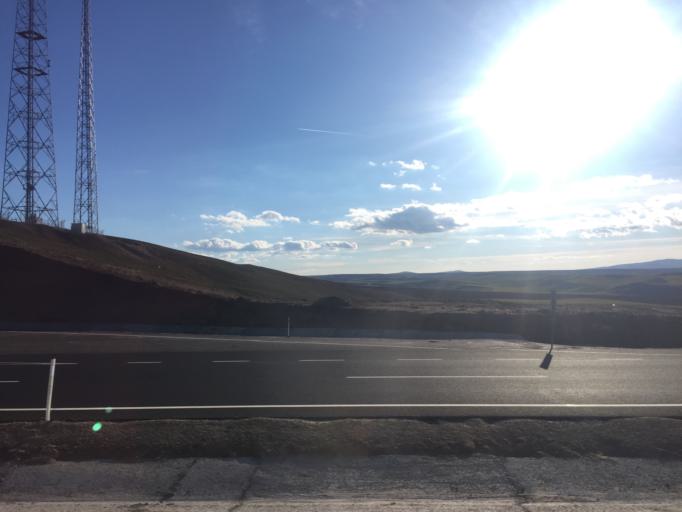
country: TR
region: Kirsehir
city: Kaman
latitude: 39.5138
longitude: 33.7739
